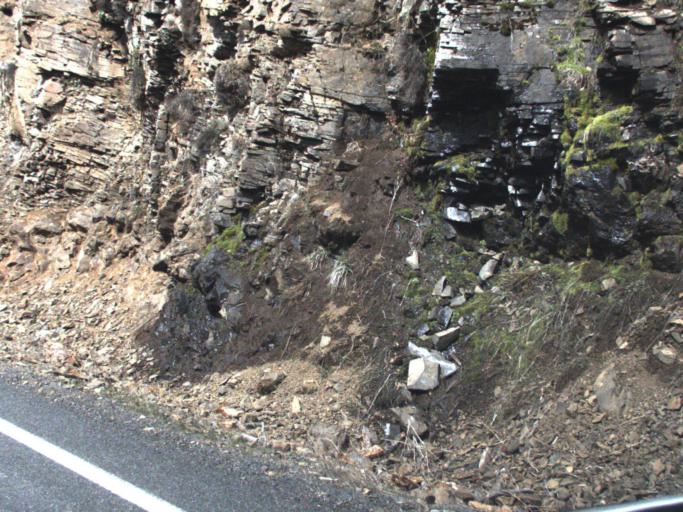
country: US
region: Washington
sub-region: Kittitas County
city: Cle Elum
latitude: 46.9739
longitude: -121.1962
